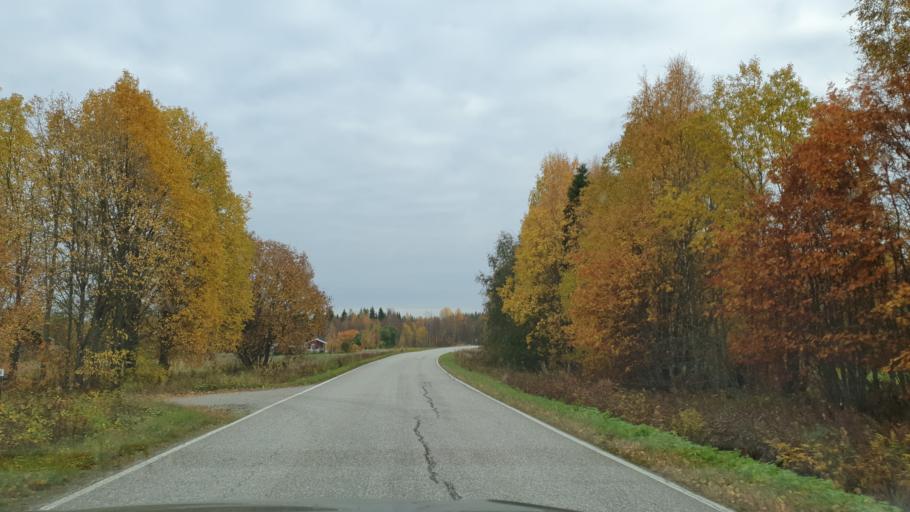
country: FI
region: Kainuu
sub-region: Kajaani
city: Ristijaervi
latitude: 64.4681
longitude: 28.3037
